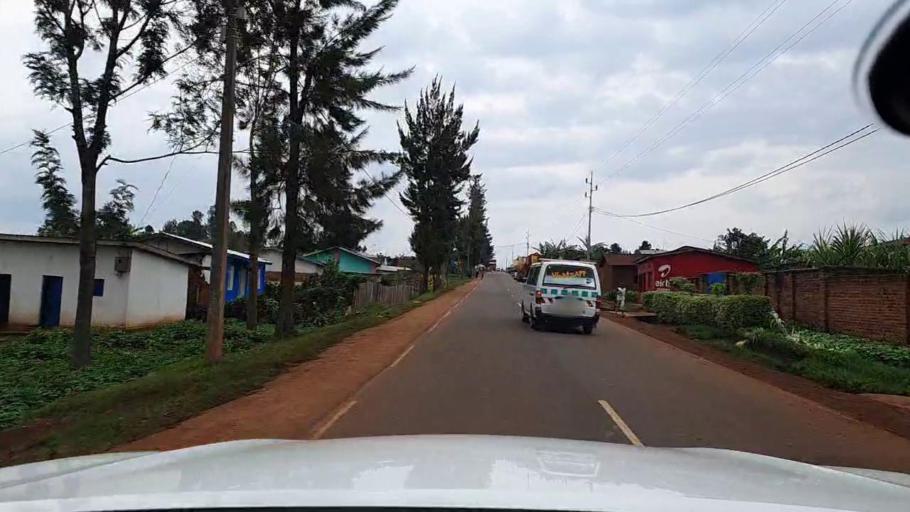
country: RW
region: Western Province
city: Cyangugu
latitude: -2.6340
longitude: 28.9520
